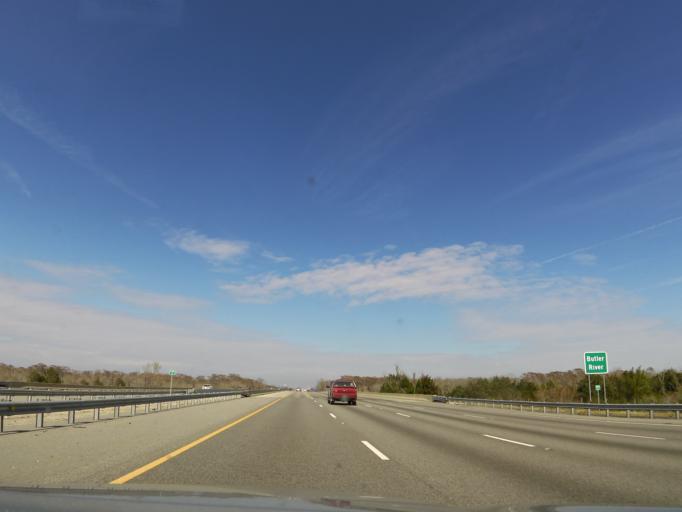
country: US
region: Georgia
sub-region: McIntosh County
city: Darien
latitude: 31.3616
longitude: -81.4582
